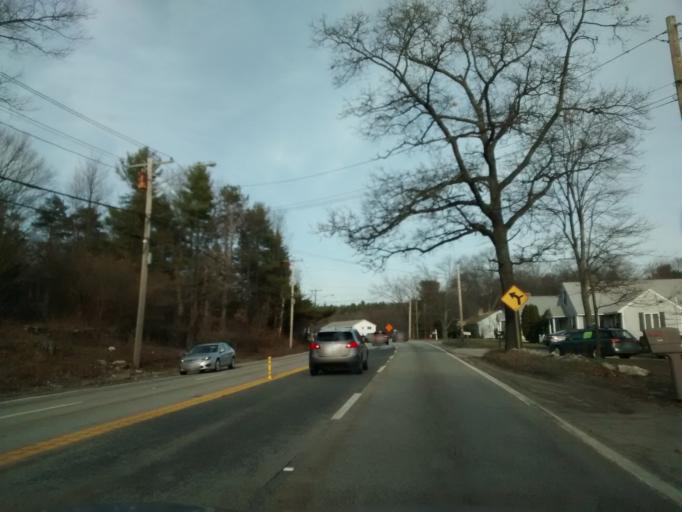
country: US
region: Massachusetts
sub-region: Worcester County
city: Oxford
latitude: 42.1681
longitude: -71.8875
